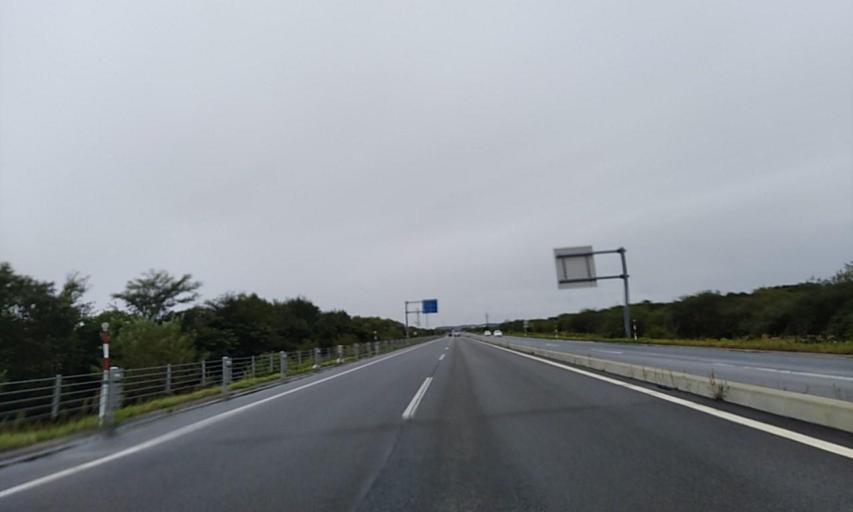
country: JP
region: Hokkaido
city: Kushiro
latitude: 43.0324
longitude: 144.3074
